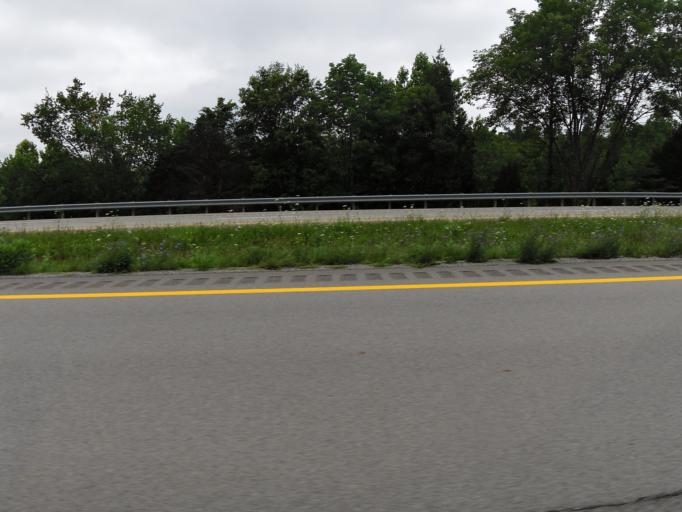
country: US
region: Kentucky
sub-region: Grayson County
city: Leitchfield
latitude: 37.4130
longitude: -86.5133
